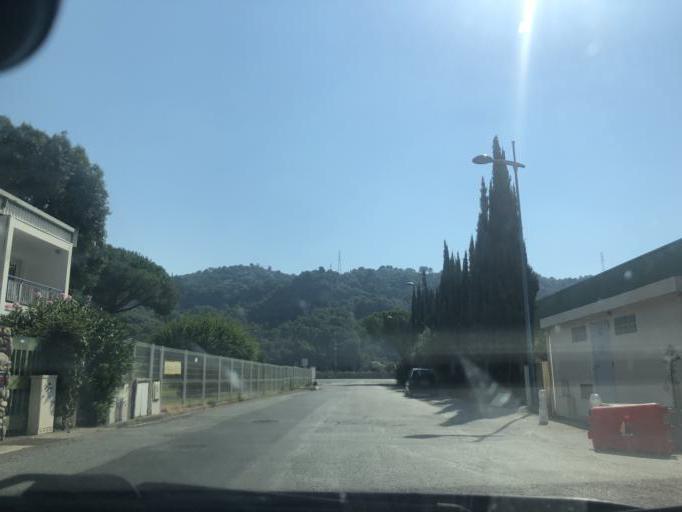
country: FR
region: Provence-Alpes-Cote d'Azur
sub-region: Departement des Alpes-Maritimes
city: Colomars
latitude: 43.7713
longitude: 7.2065
